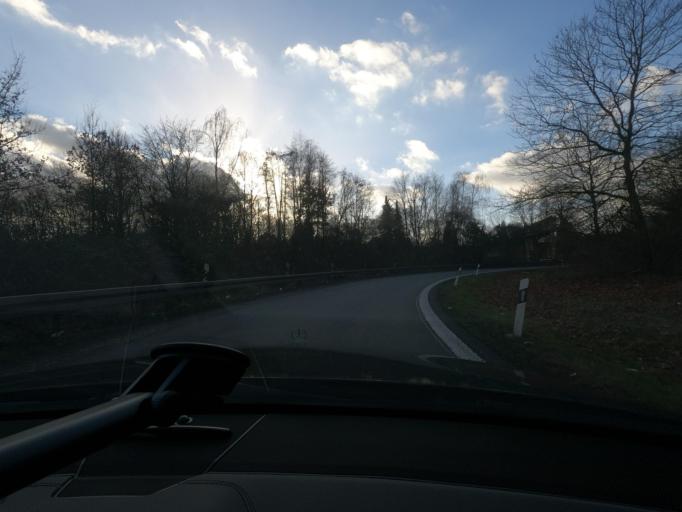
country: DE
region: North Rhine-Westphalia
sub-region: Regierungsbezirk Arnsberg
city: Dortmund
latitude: 51.4960
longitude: 7.5111
